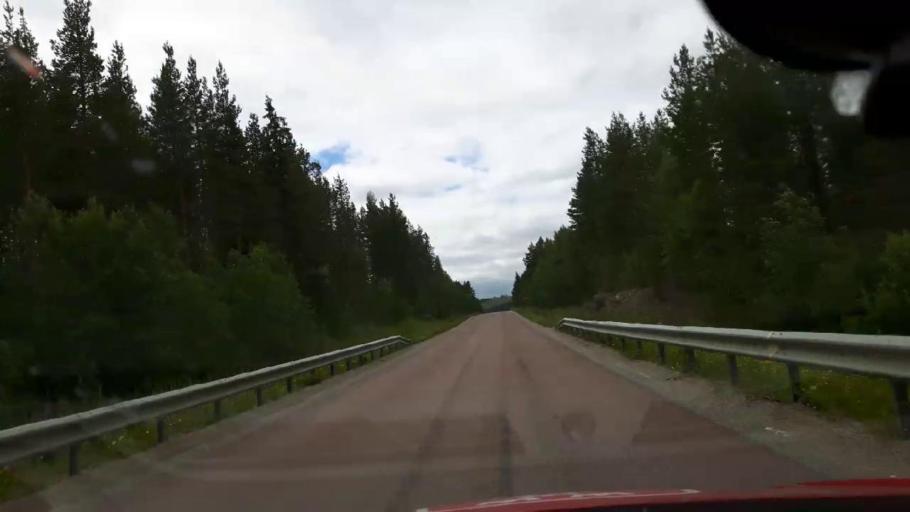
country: SE
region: Jaemtland
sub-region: Braecke Kommun
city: Braecke
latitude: 62.9054
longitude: 15.1517
